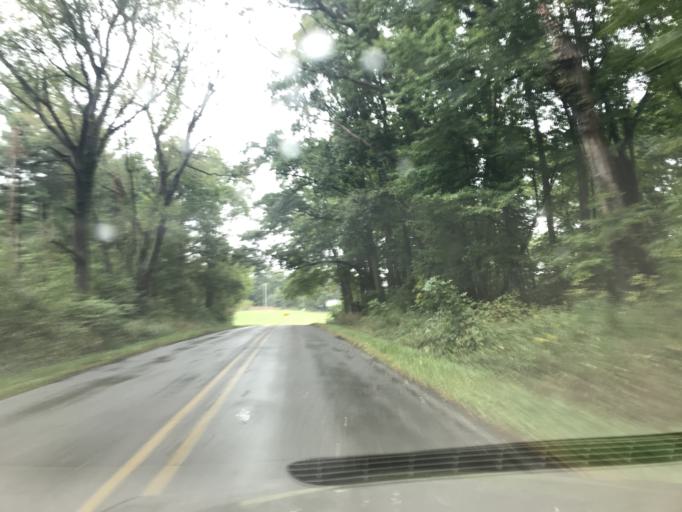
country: US
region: Michigan
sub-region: Ingham County
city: Leslie
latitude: 42.3632
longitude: -84.5478
